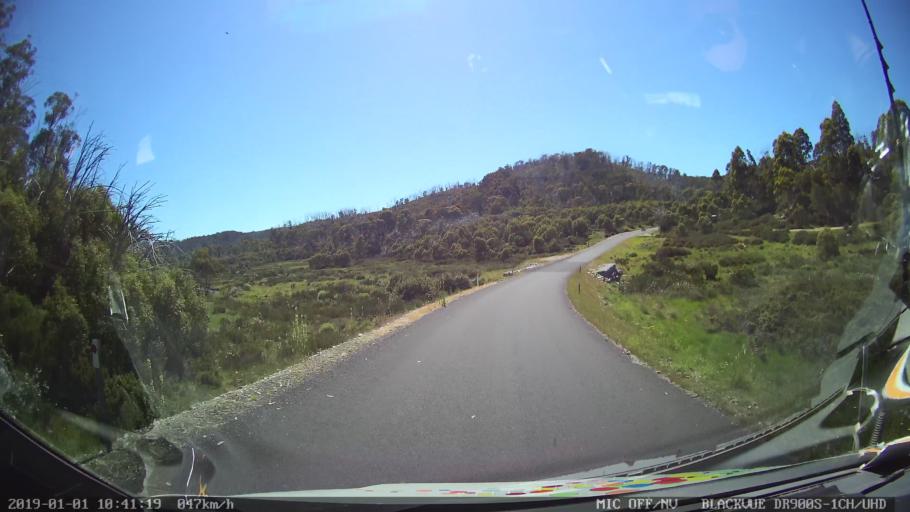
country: AU
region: New South Wales
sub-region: Snowy River
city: Jindabyne
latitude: -36.0367
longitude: 148.3193
